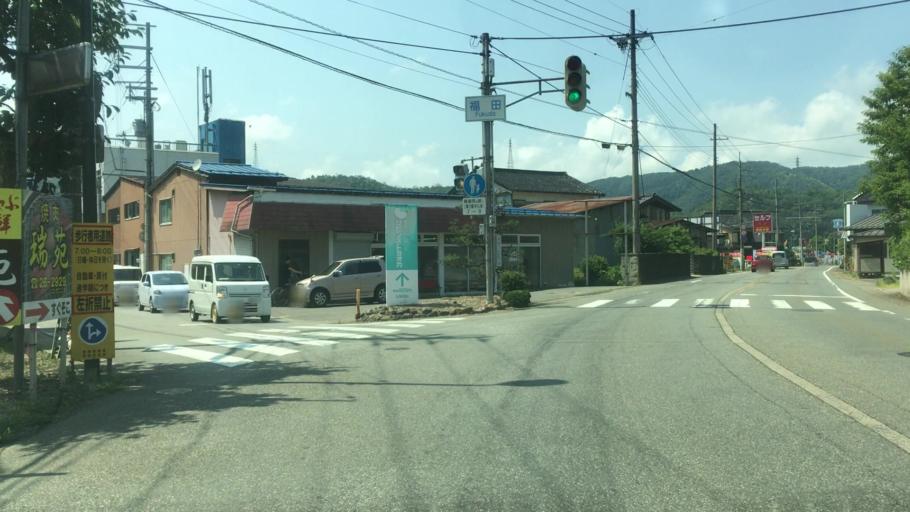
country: JP
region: Hyogo
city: Toyooka
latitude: 35.5549
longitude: 134.7980
